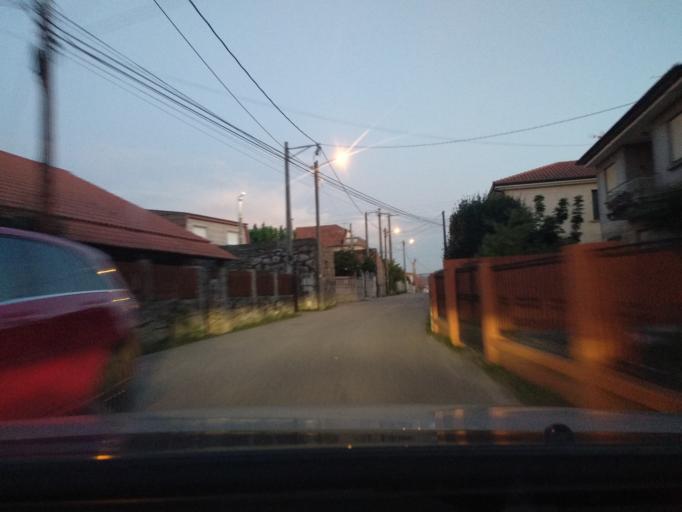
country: ES
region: Galicia
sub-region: Provincia de Pontevedra
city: Moana
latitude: 42.2841
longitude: -8.7483
